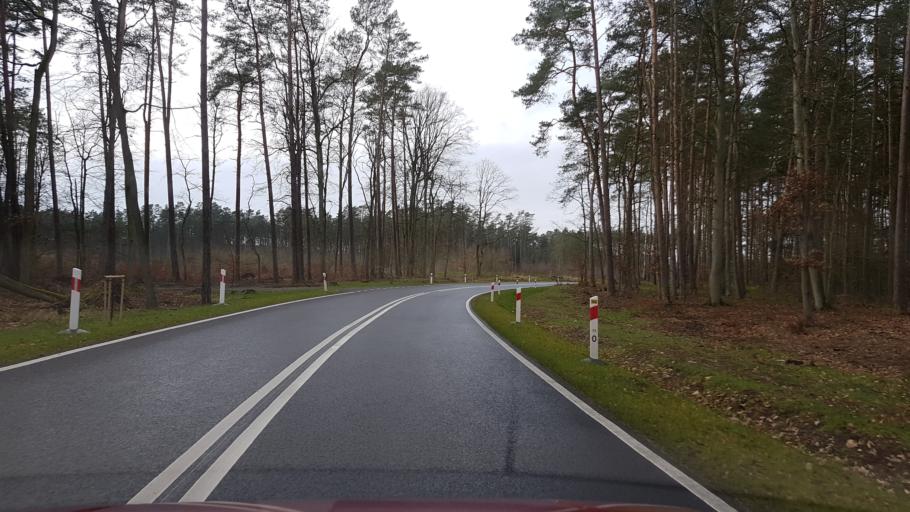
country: PL
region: West Pomeranian Voivodeship
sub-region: Powiat policki
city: Nowe Warpno
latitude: 53.6710
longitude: 14.4018
